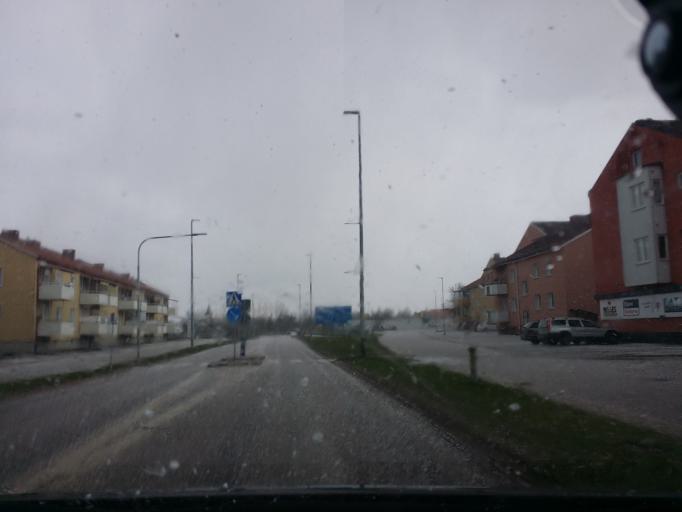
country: SE
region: Vaestmanland
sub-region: Sala Kommun
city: Sala
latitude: 59.9169
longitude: 16.6116
